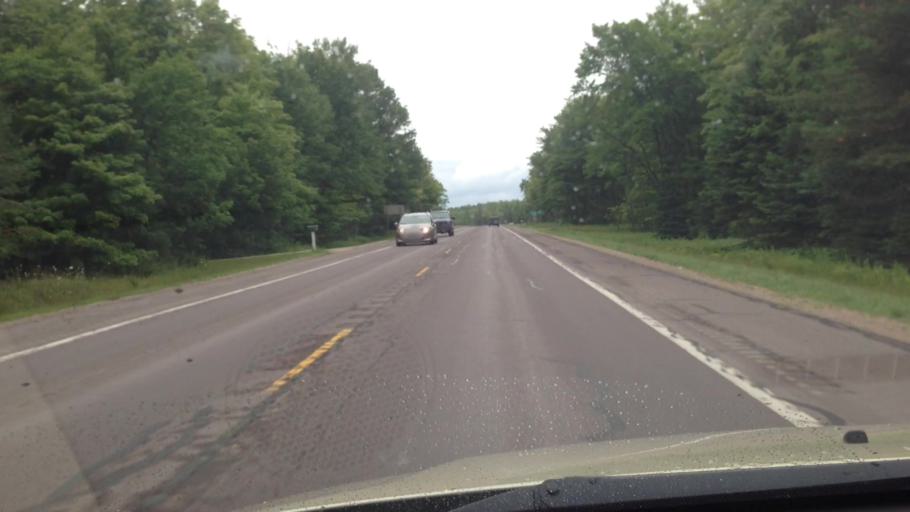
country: US
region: Michigan
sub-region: Schoolcraft County
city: Manistique
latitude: 46.0530
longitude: -85.9634
